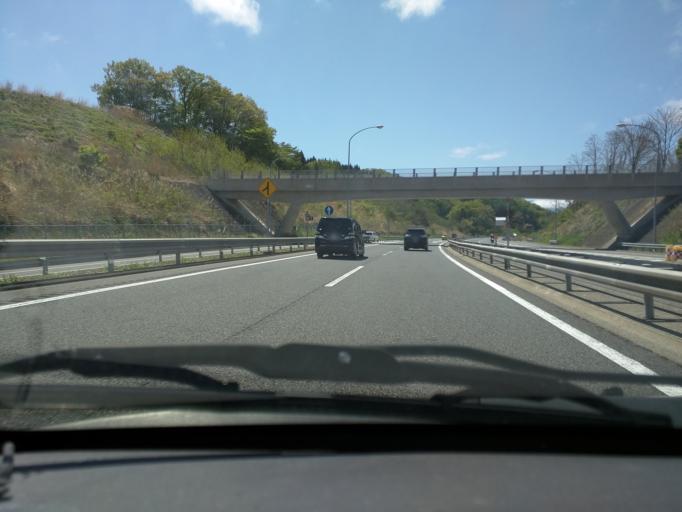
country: JP
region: Nagano
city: Nakano
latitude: 36.7957
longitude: 138.3218
